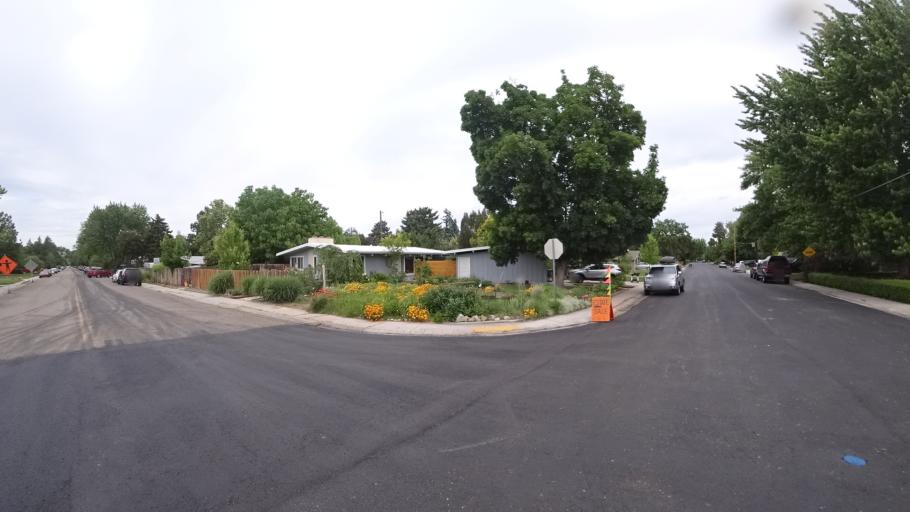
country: US
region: Idaho
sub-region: Ada County
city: Boise
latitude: 43.5771
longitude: -116.2037
